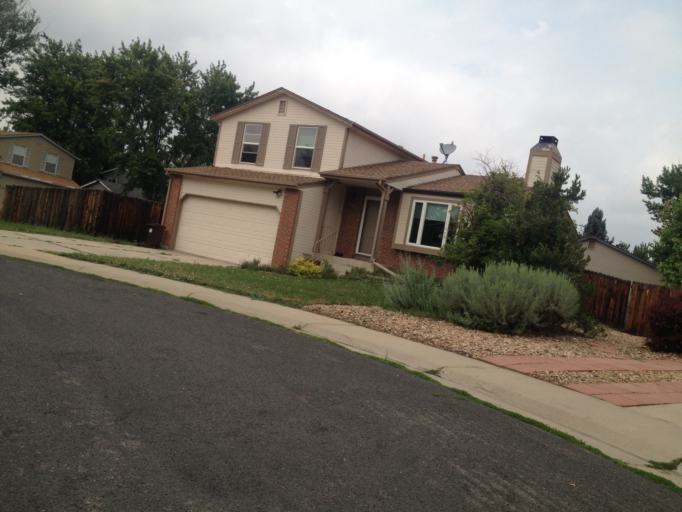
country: US
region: Colorado
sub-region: Boulder County
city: Louisville
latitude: 39.9667
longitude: -105.1371
